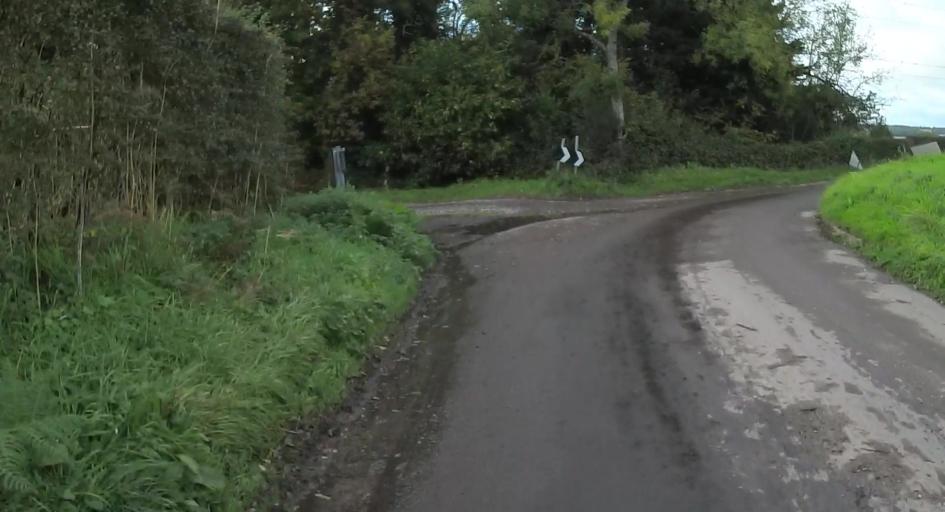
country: GB
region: England
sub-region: Hampshire
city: Alton
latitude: 51.1551
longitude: -0.9262
